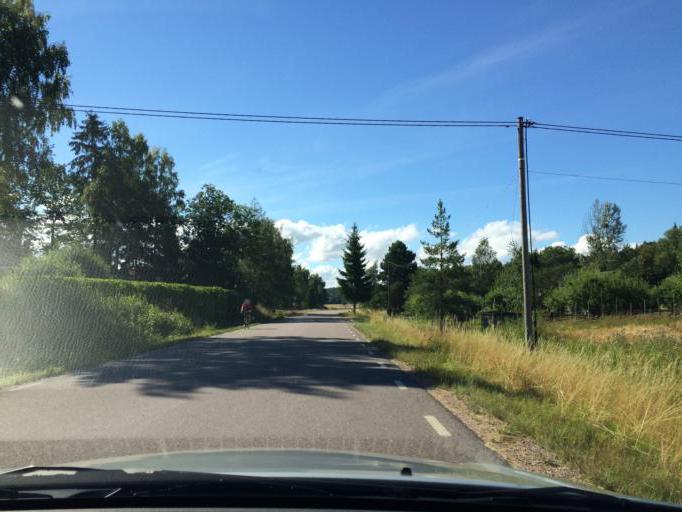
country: SE
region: Soedermanland
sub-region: Eskilstuna Kommun
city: Torshalla
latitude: 59.5196
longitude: 16.4375
